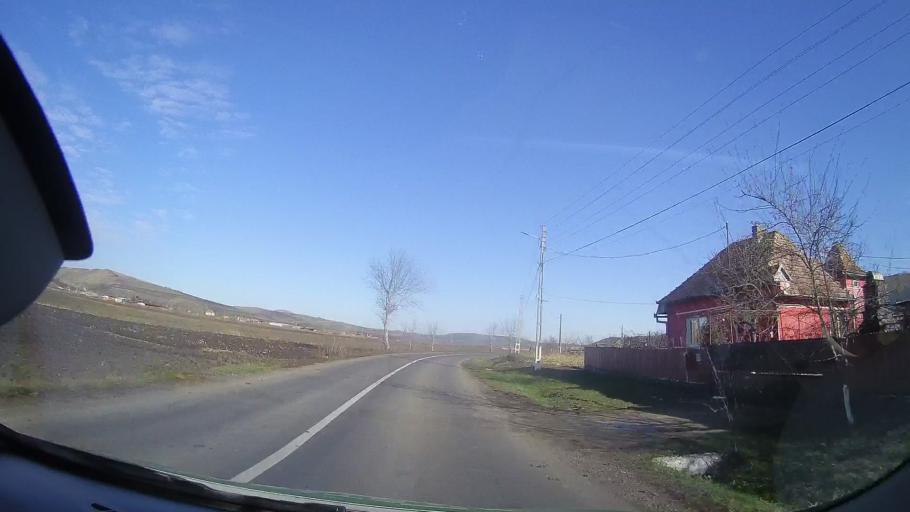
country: RO
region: Mures
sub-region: Comuna Grebenisu de Campie
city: Grebenisu de Campie
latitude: 46.5611
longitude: 24.3346
